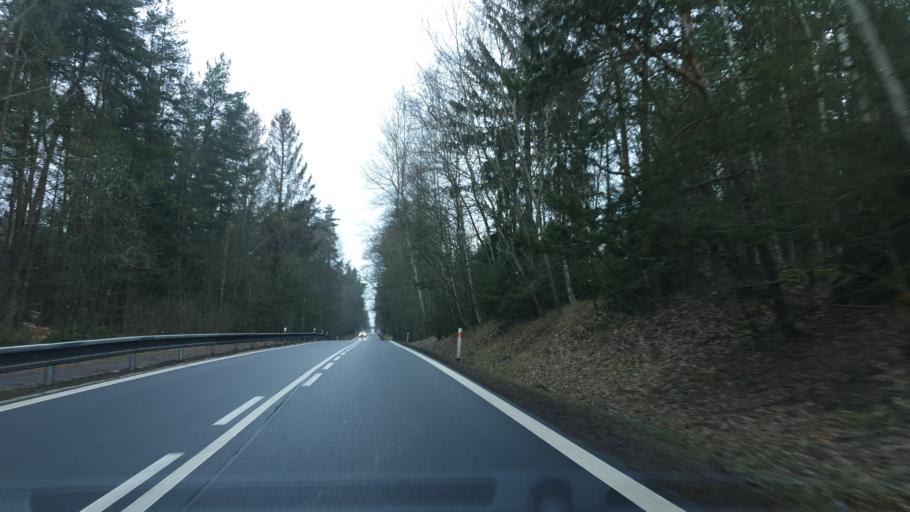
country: CZ
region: Karlovarsky
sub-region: Okres Cheb
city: Frantiskovy Lazne
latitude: 50.1456
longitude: 12.3313
